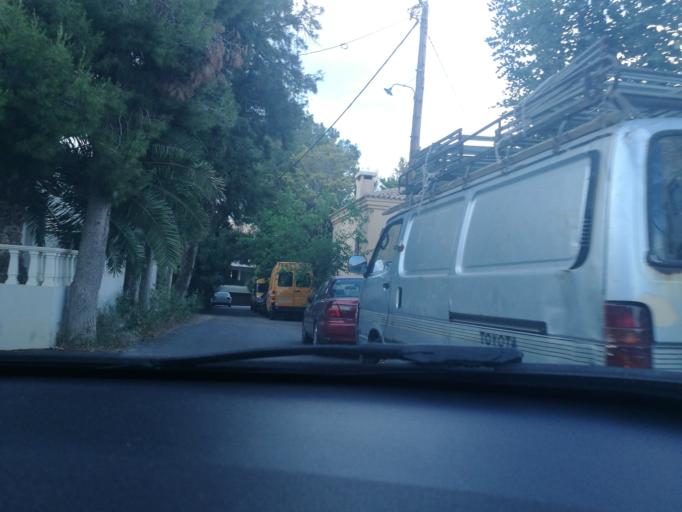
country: GR
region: Crete
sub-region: Nomos Irakleiou
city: Irakleion
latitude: 35.3165
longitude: 25.1494
